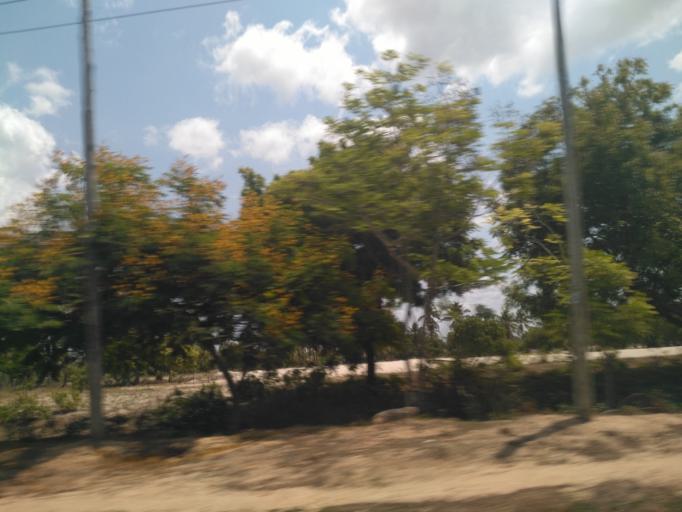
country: TZ
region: Dar es Salaam
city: Dar es Salaam
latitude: -6.8263
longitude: 39.3281
